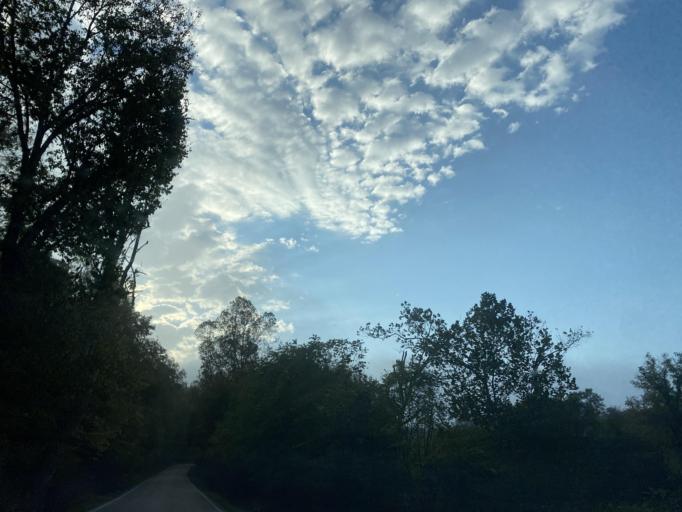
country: US
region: Kentucky
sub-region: Pendleton County
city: Falmouth
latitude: 38.7498
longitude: -84.3214
